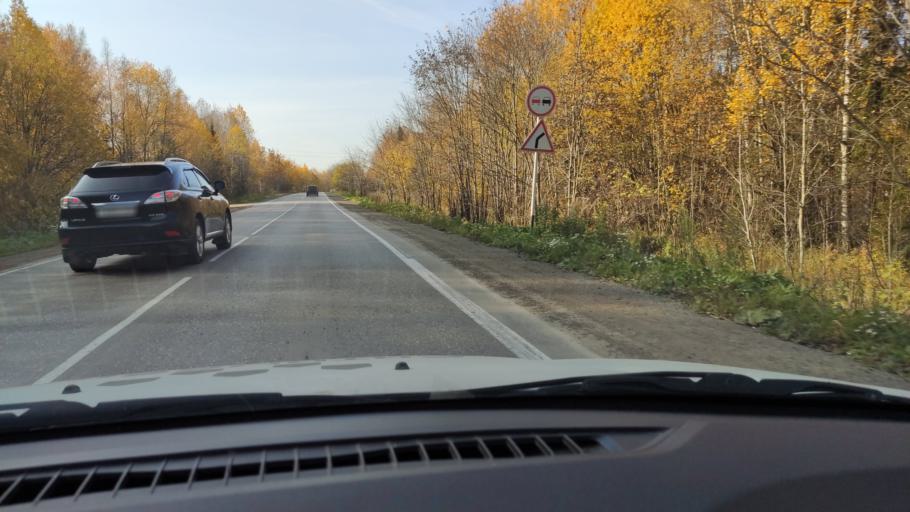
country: RU
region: Perm
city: Novyye Lyady
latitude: 58.0209
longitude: 56.6479
